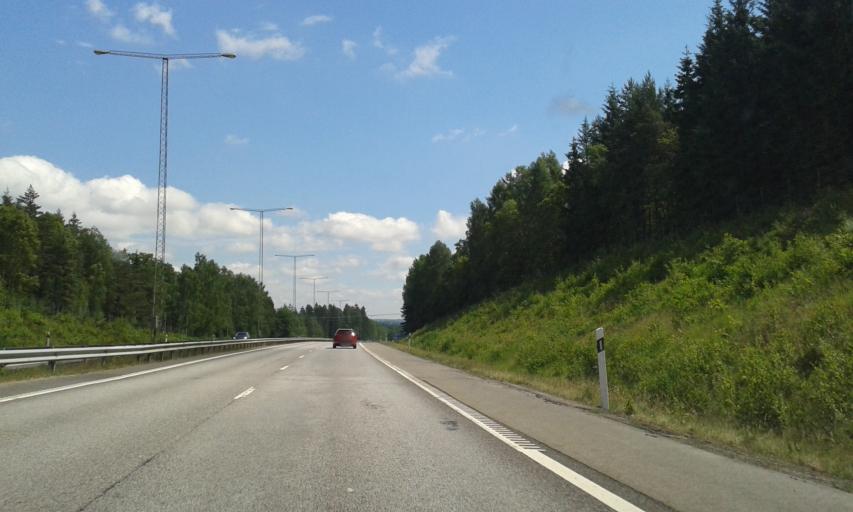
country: SE
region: Kronoberg
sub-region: Vaxjo Kommun
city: Vaexjoe
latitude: 56.8980
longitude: 14.7216
